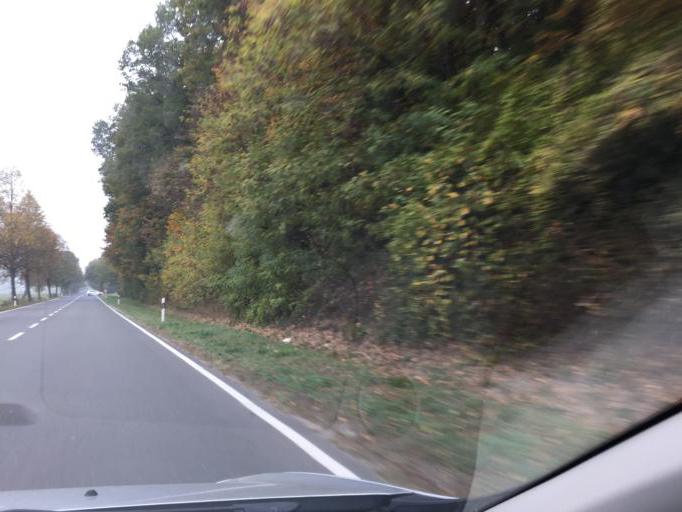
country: LU
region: Grevenmacher
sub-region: Canton de Remich
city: Waldbredimus
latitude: 49.5612
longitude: 6.3036
